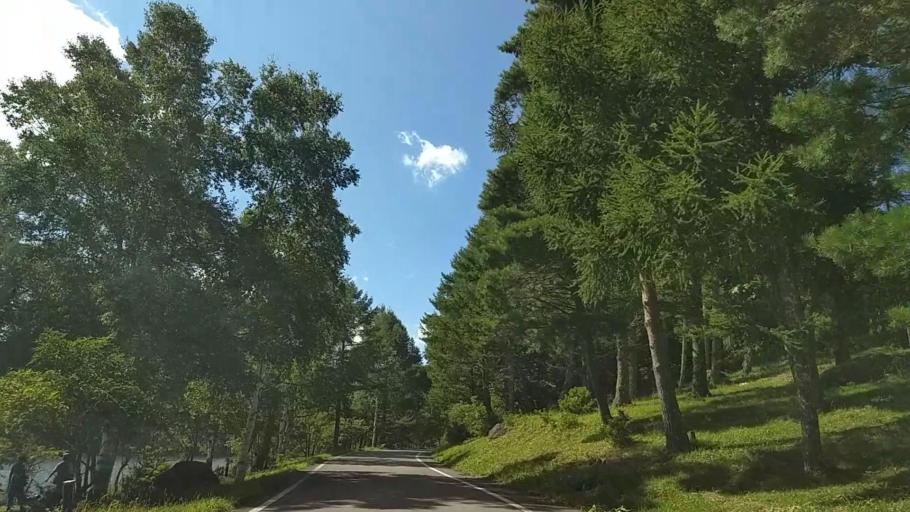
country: JP
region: Nagano
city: Kamimaruko
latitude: 36.1377
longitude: 138.2692
